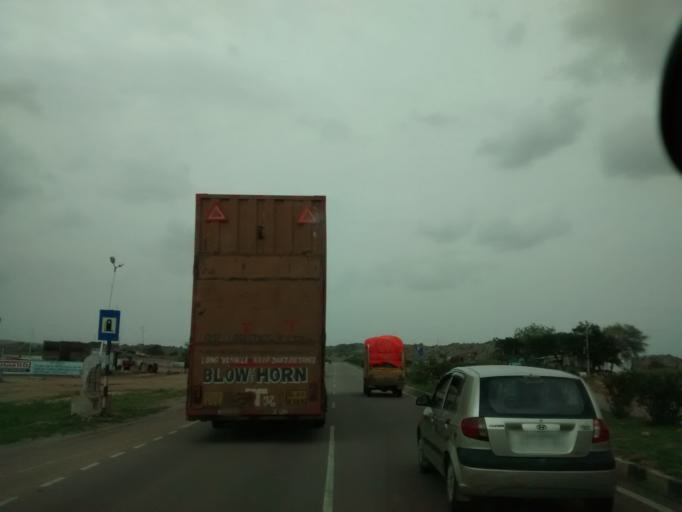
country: IN
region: Andhra Pradesh
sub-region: Kurnool
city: Ramapuram
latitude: 15.1752
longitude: 77.6852
